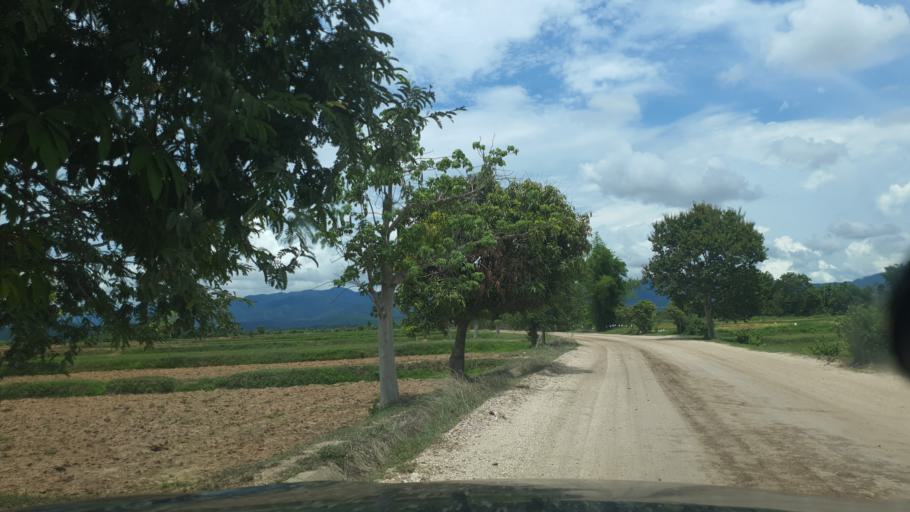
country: TH
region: Lampang
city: Sop Prap
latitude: 17.9388
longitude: 99.3583
